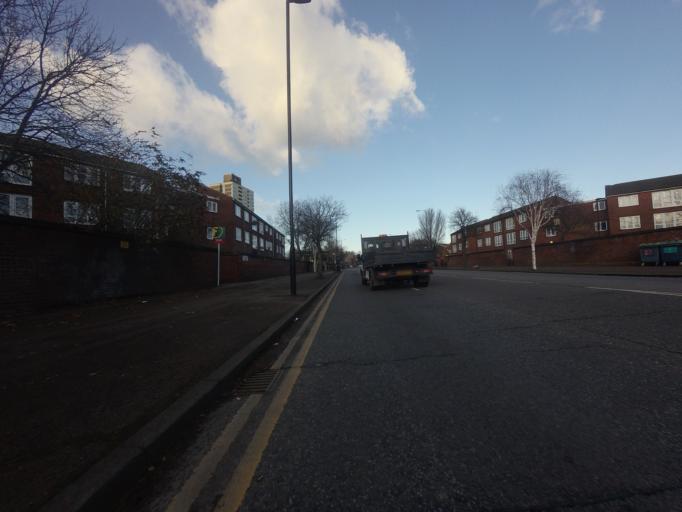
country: GB
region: England
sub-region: Greater London
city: Poplar
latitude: 51.5327
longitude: 0.0077
